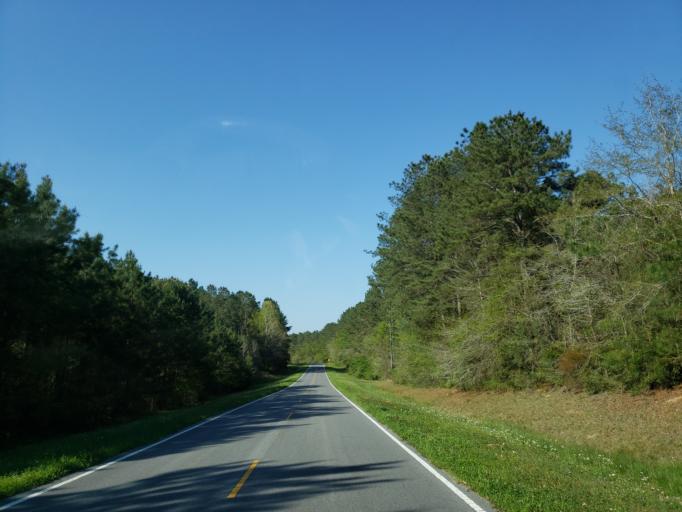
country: US
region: Mississippi
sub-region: Covington County
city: Collins
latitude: 31.6830
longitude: -89.4132
